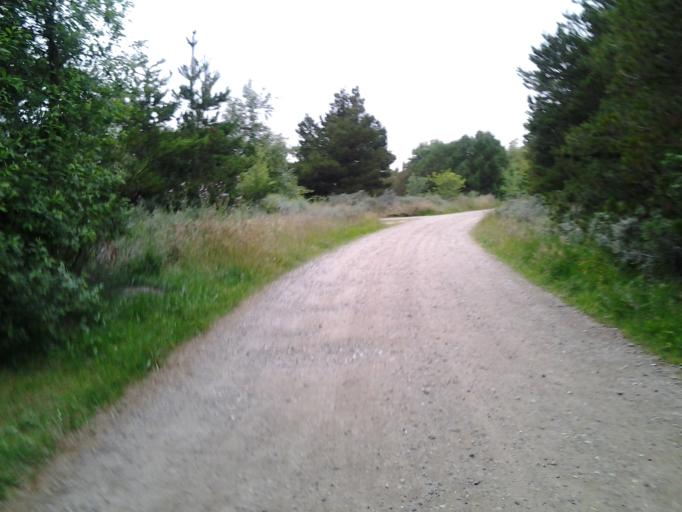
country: DE
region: Schleswig-Holstein
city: List
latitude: 55.1544
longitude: 8.5234
